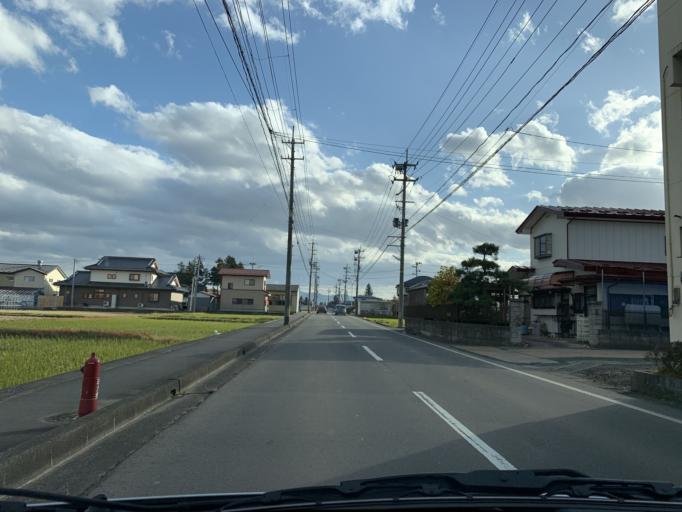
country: JP
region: Iwate
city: Mizusawa
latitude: 39.1500
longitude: 141.1589
